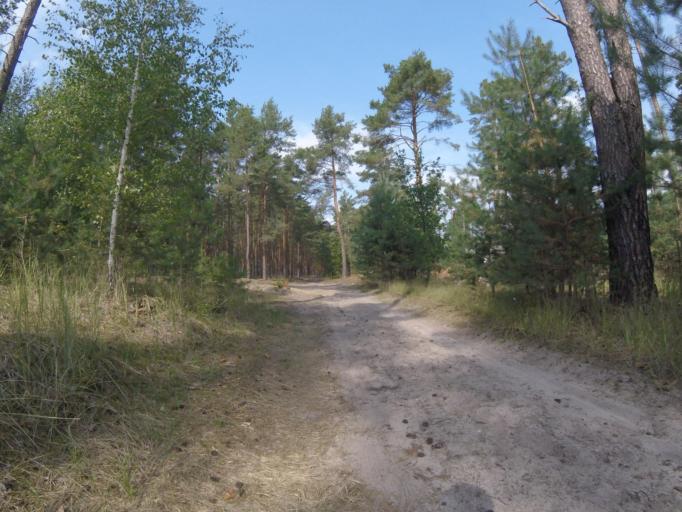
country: DE
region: Brandenburg
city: Bestensee
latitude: 52.2777
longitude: 13.6692
